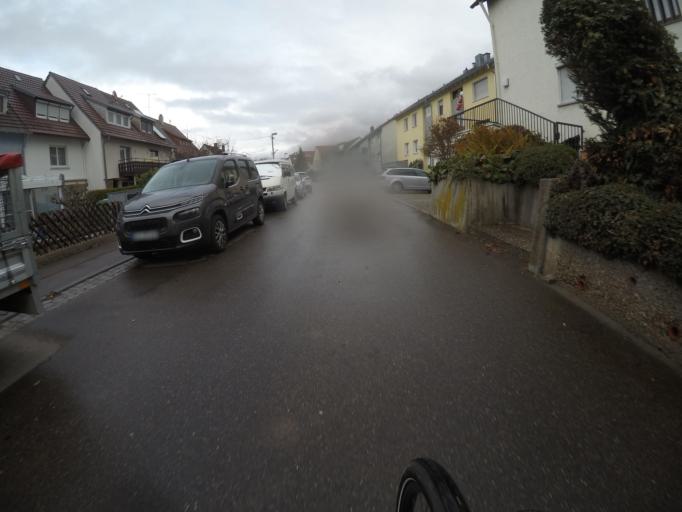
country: DE
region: Baden-Wuerttemberg
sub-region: Regierungsbezirk Stuttgart
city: Gerlingen
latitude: 48.7974
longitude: 9.0695
